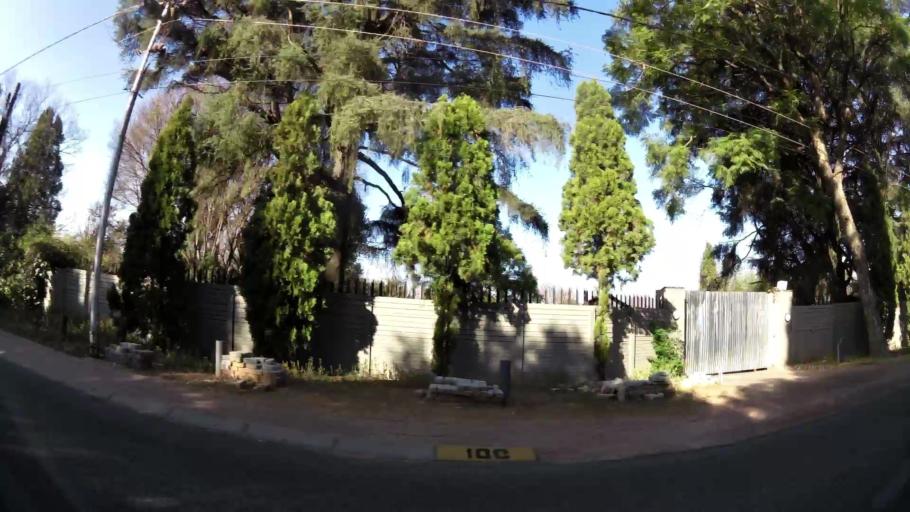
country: ZA
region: Gauteng
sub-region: City of Johannesburg Metropolitan Municipality
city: Johannesburg
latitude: -26.1100
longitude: 28.0708
